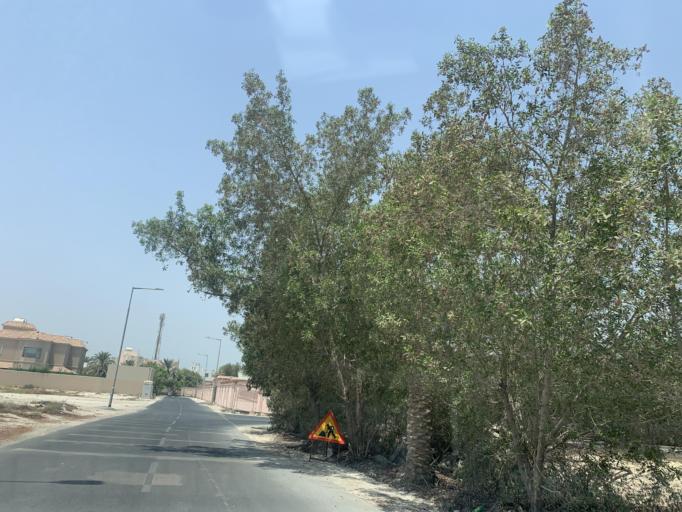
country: BH
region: Manama
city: Jidd Hafs
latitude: 26.2083
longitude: 50.4753
